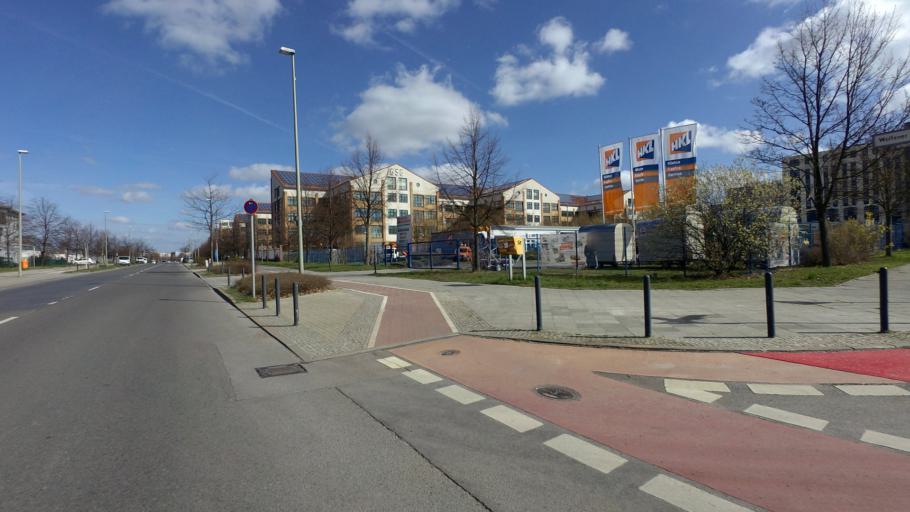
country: DE
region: Berlin
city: Falkenberg
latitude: 52.5589
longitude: 13.5498
